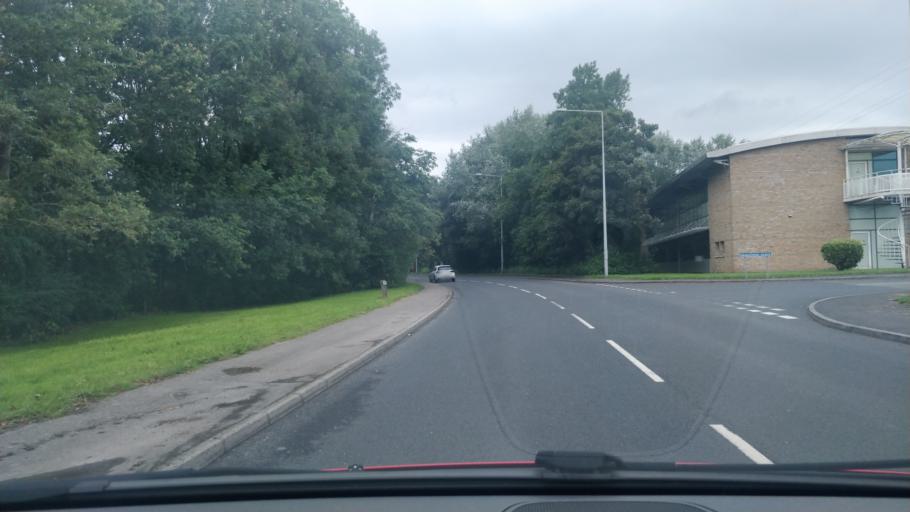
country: GB
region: England
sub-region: Lancashire
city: Leyland
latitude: 53.7021
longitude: -2.7270
